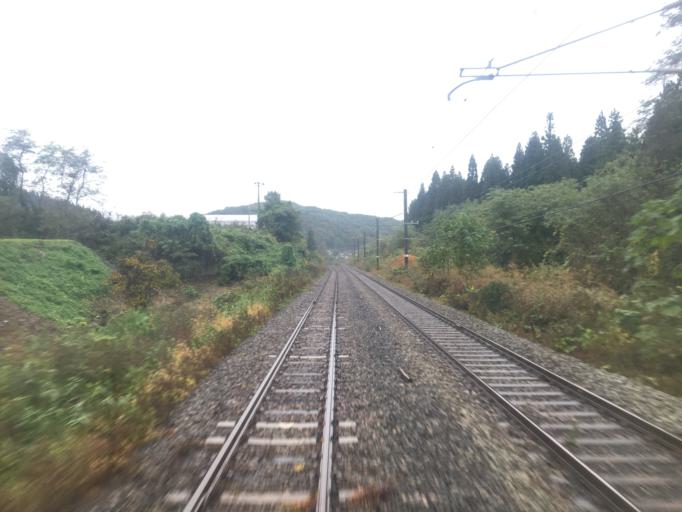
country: JP
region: Yamagata
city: Shinjo
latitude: 38.7295
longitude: 140.3109
